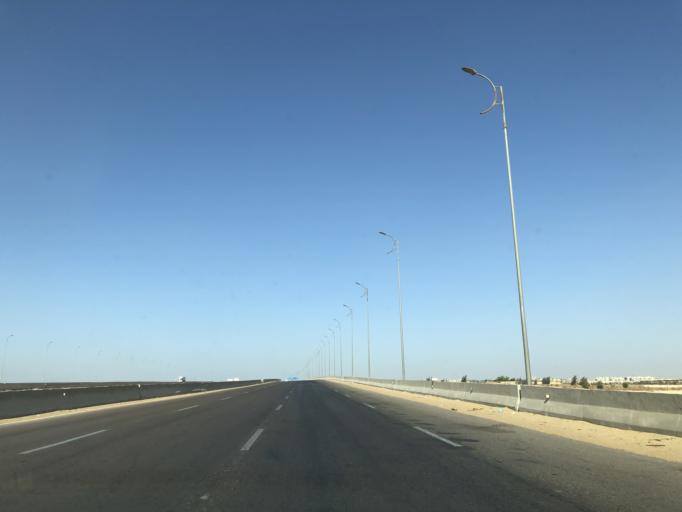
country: EG
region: Al Jizah
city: Awsim
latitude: 30.0718
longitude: 30.9154
